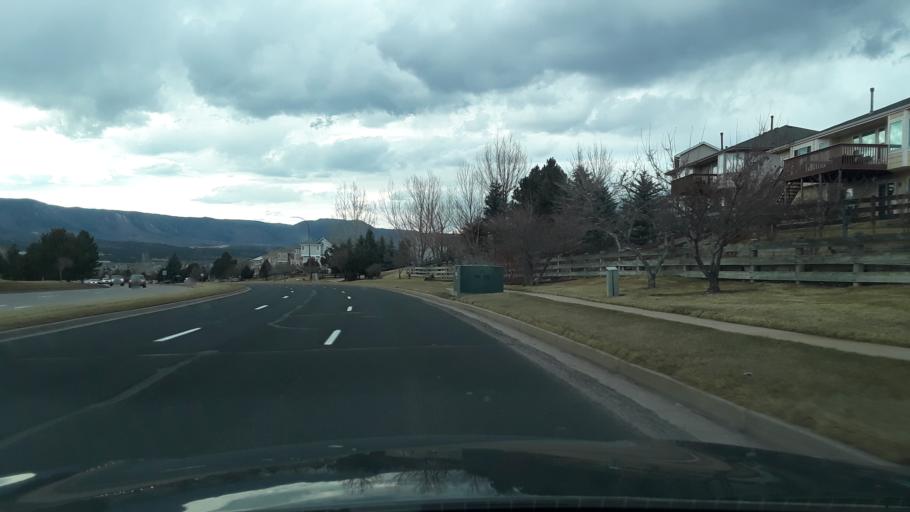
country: US
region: Colorado
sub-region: El Paso County
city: Gleneagle
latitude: 39.0070
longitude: -104.7981
